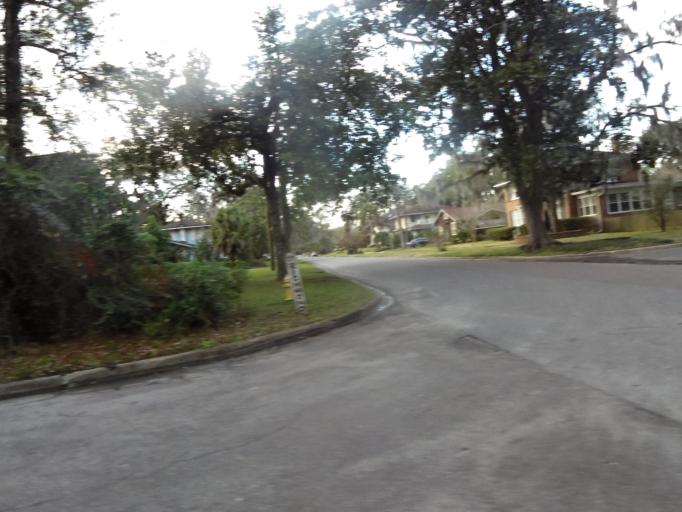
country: US
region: Florida
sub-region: Duval County
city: Jacksonville
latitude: 30.2894
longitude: -81.7063
